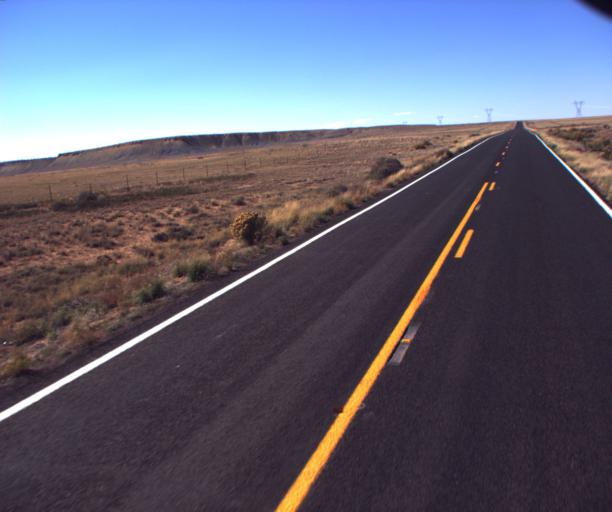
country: US
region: Arizona
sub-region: Coconino County
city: Tuba City
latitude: 35.9707
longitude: -110.8262
